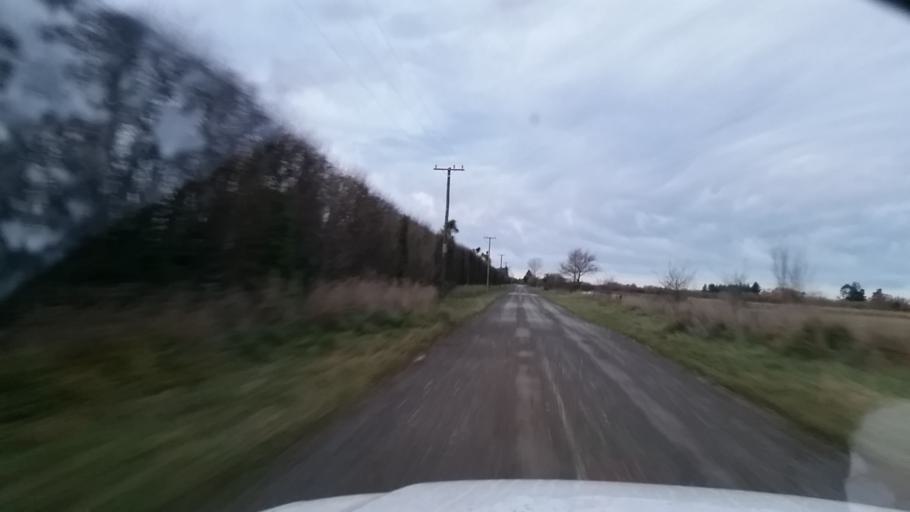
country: NZ
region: Canterbury
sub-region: Ashburton District
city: Ashburton
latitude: -43.8470
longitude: 171.6514
